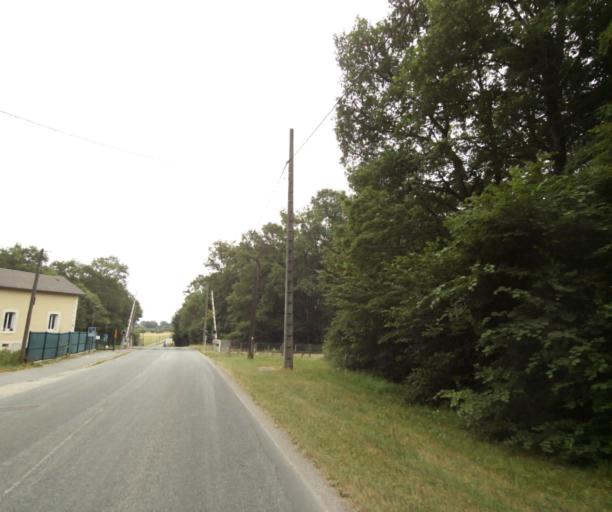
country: FR
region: Centre
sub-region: Departement du Loiret
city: Marigny-les-Usages
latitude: 47.9607
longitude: 2.0007
